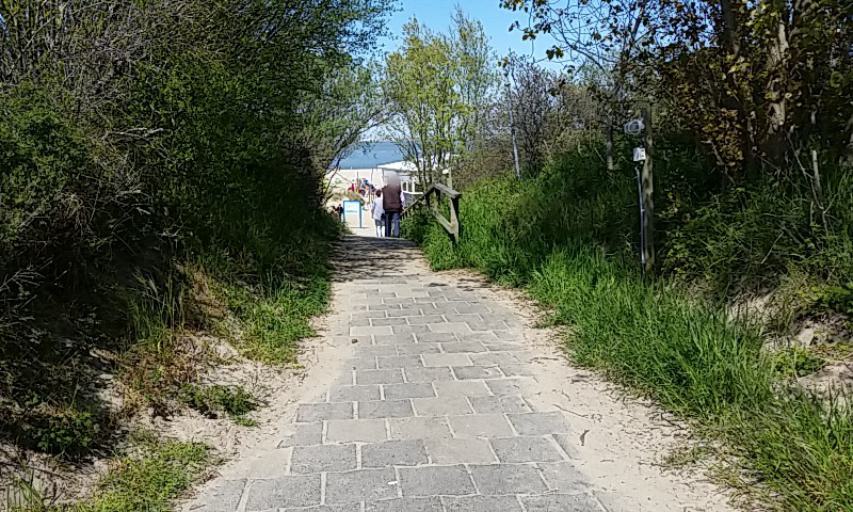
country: NL
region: Zeeland
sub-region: Gemeente Vlissingen
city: Vlissingen
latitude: 51.3981
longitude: 3.5594
